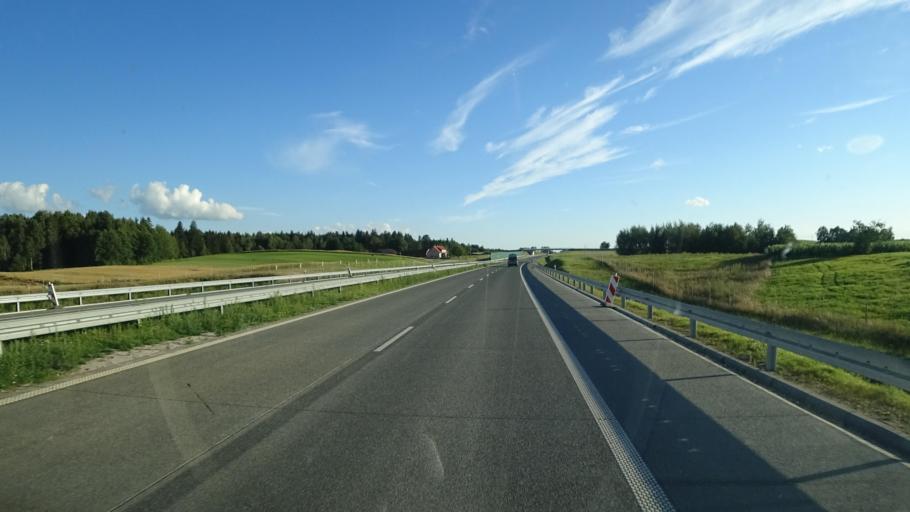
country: PL
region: Podlasie
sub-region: Powiat suwalski
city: Raczki
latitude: 53.9300
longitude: 22.7563
